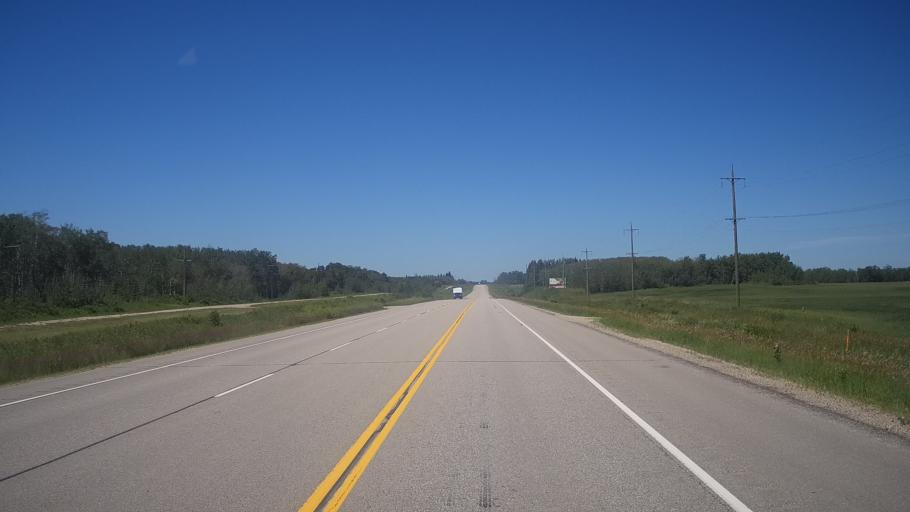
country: CA
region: Manitoba
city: Neepawa
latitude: 50.2253
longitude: -99.3511
